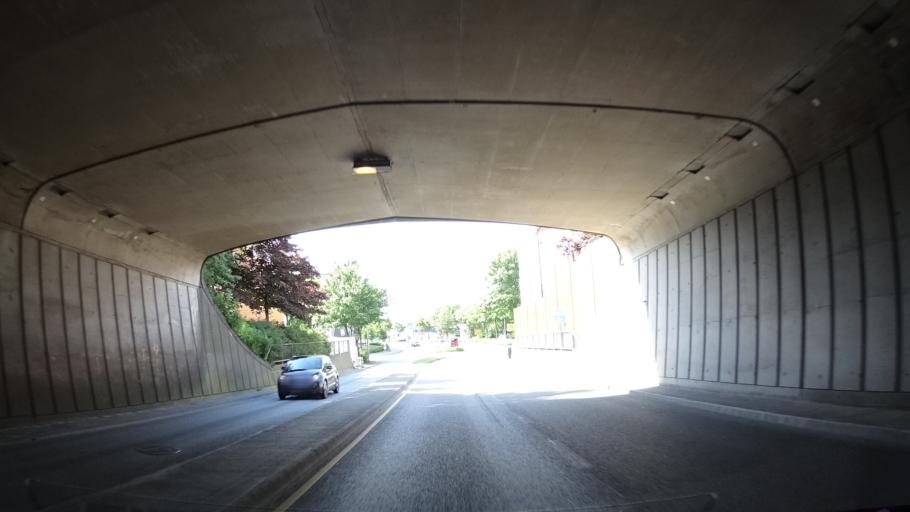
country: NO
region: Rogaland
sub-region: Stavanger
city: Stavanger
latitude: 58.9703
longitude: 5.7475
